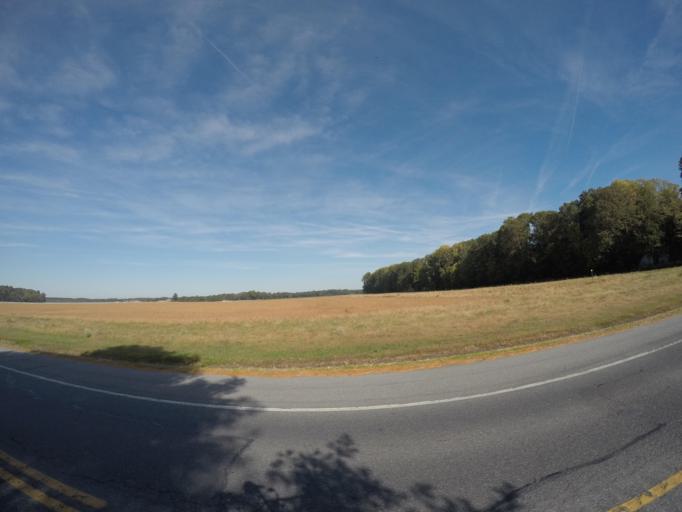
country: US
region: Delaware
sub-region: Sussex County
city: Milton
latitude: 38.7873
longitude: -75.3277
